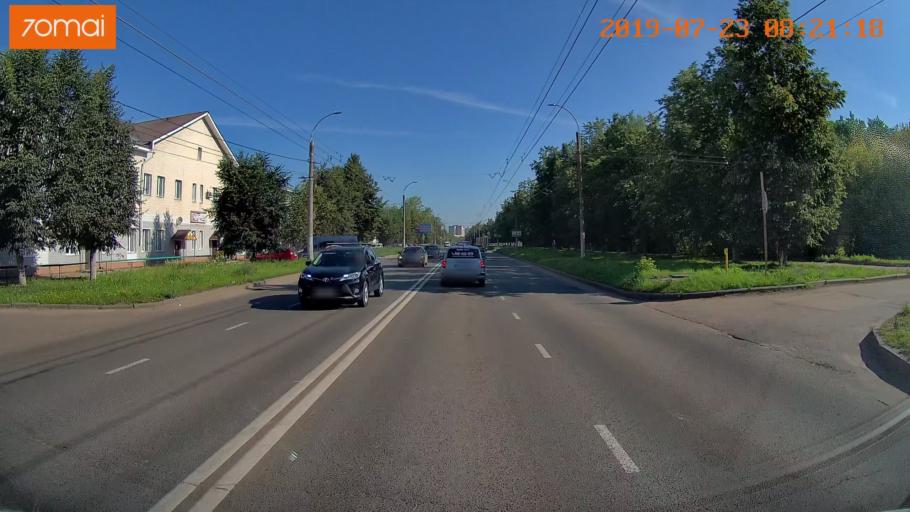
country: RU
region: Ivanovo
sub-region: Gorod Ivanovo
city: Ivanovo
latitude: 56.9750
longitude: 40.9654
